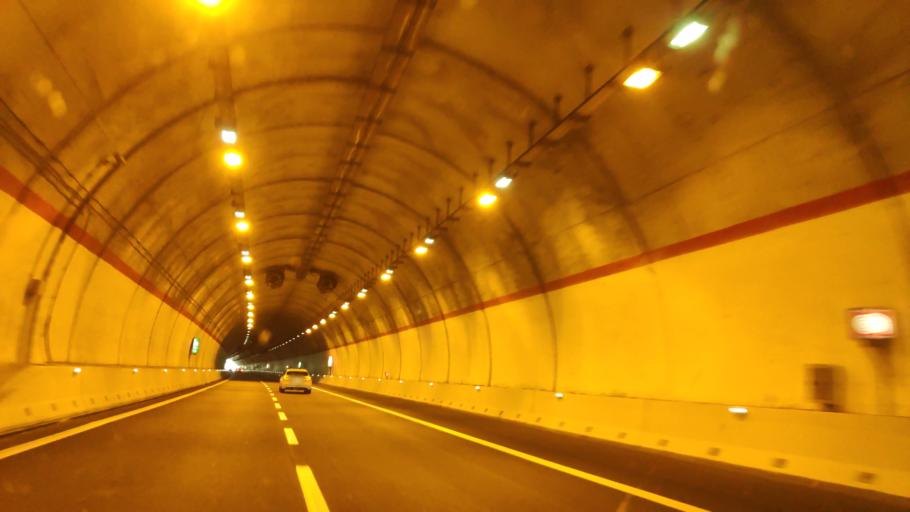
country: IT
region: Campania
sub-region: Provincia di Salerno
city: Buonabitacolo
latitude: 40.2551
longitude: 15.6605
